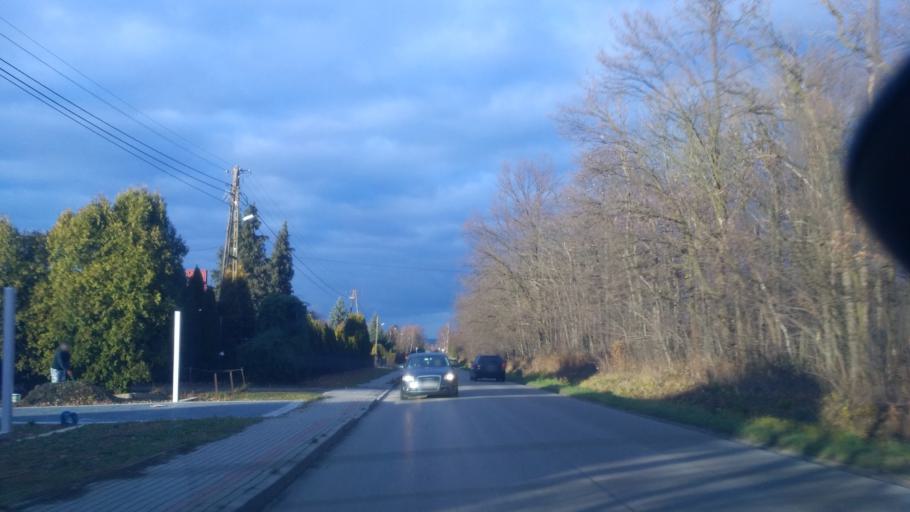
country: PL
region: Subcarpathian Voivodeship
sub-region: Powiat rzeszowski
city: Krasne
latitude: 50.0500
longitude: 22.1225
